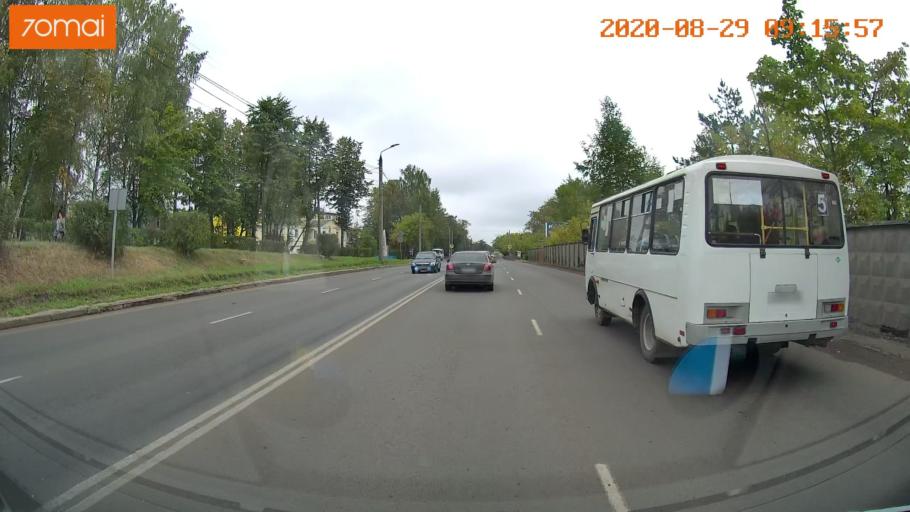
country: RU
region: Ivanovo
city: Kineshma
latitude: 57.4400
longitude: 42.1354
